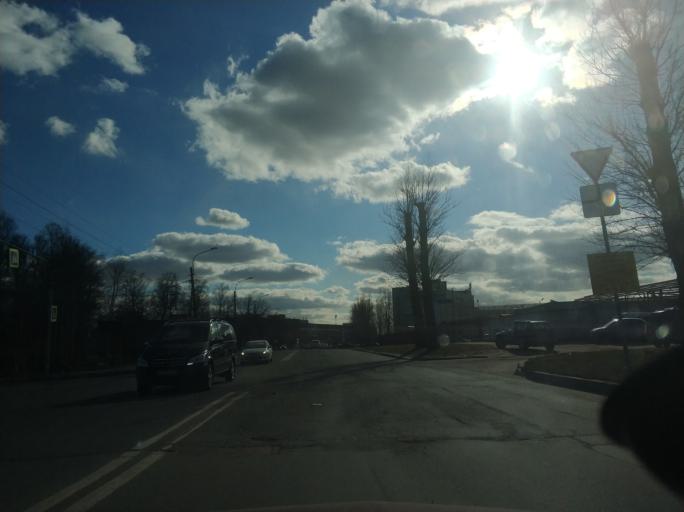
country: RU
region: St.-Petersburg
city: Krasnogvargeisky
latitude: 59.9654
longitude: 30.4691
